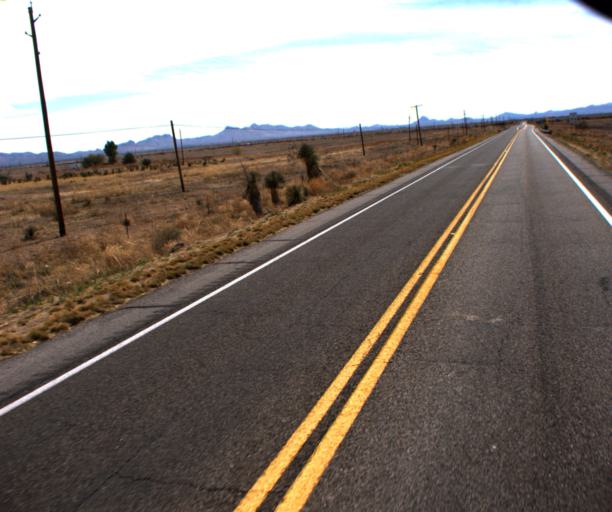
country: US
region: Arizona
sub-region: Cochise County
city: Pirtleville
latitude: 31.4488
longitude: -109.6036
